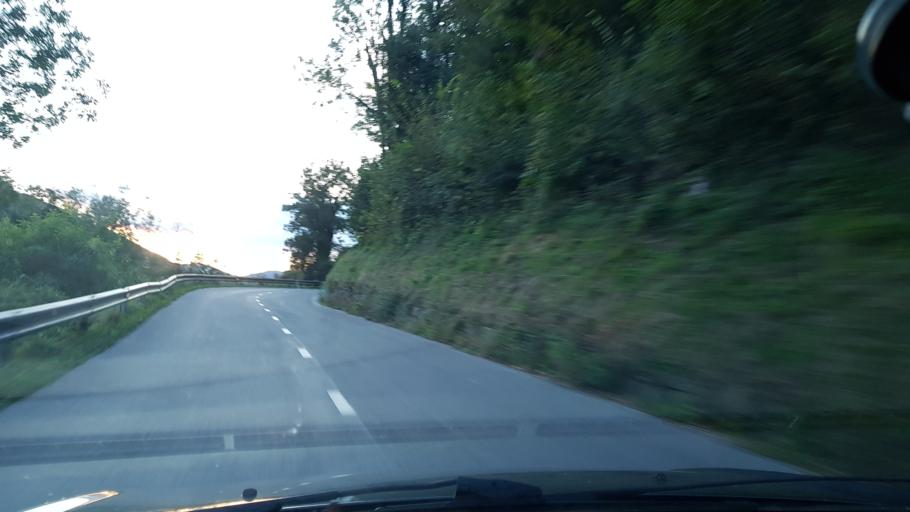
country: SI
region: Kobarid
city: Kobarid
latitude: 46.2495
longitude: 13.5195
